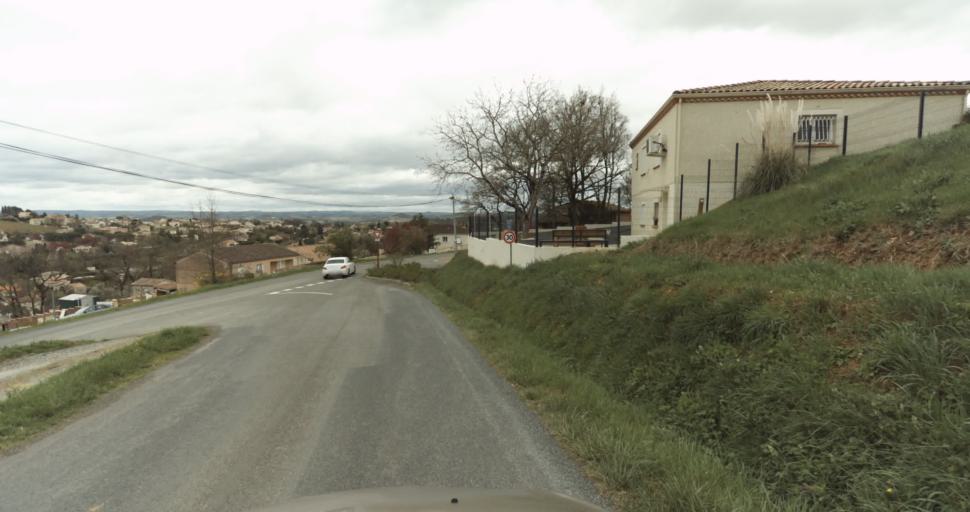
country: FR
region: Midi-Pyrenees
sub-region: Departement du Tarn
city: Puygouzon
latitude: 43.9001
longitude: 2.1679
